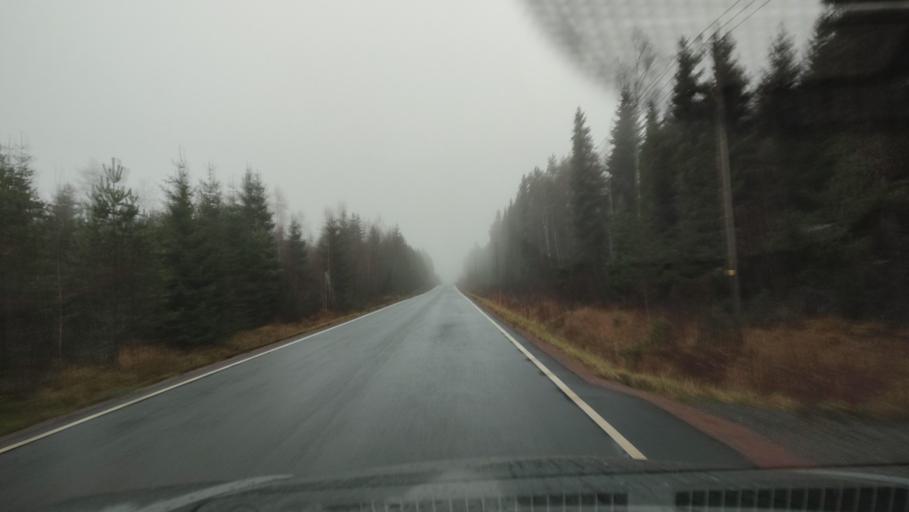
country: FI
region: Southern Ostrobothnia
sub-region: Suupohja
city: Karijoki
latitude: 62.1667
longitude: 21.7419
